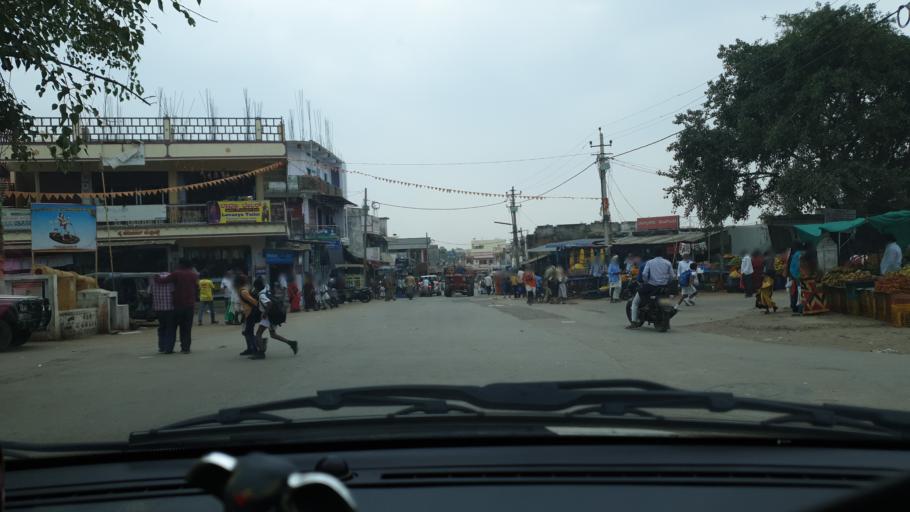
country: IN
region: Karnataka
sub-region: Yadgir
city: Gurmatkal
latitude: 16.8712
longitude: 77.3912
